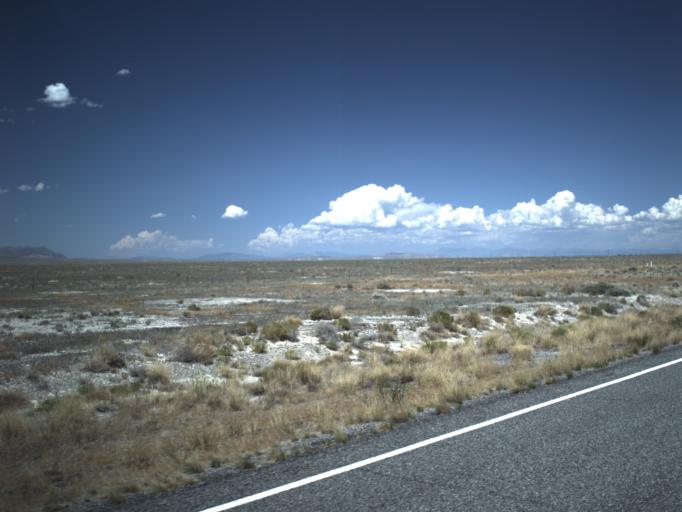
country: US
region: Utah
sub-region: Millard County
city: Delta
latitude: 39.2181
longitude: -112.9529
